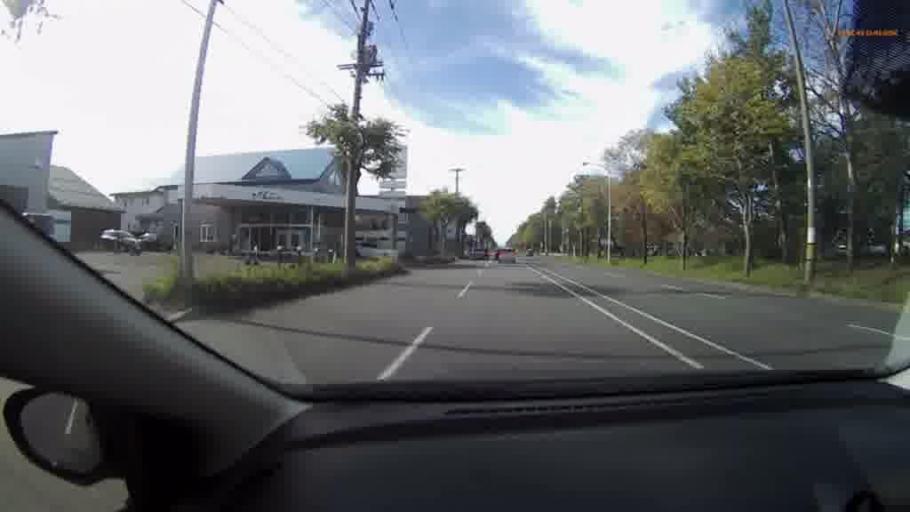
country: JP
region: Hokkaido
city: Kushiro
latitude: 43.0196
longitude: 144.4140
